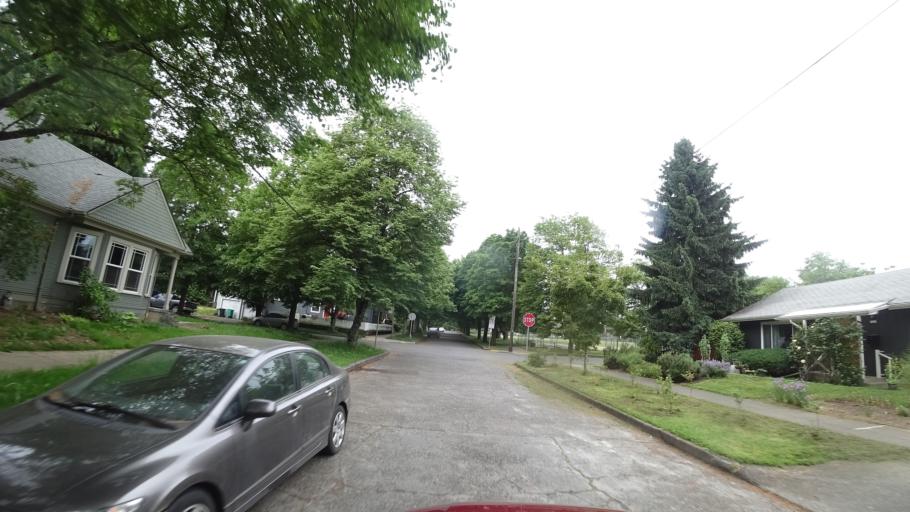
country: US
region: Oregon
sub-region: Clackamas County
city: Milwaukie
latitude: 45.4615
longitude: -122.6486
